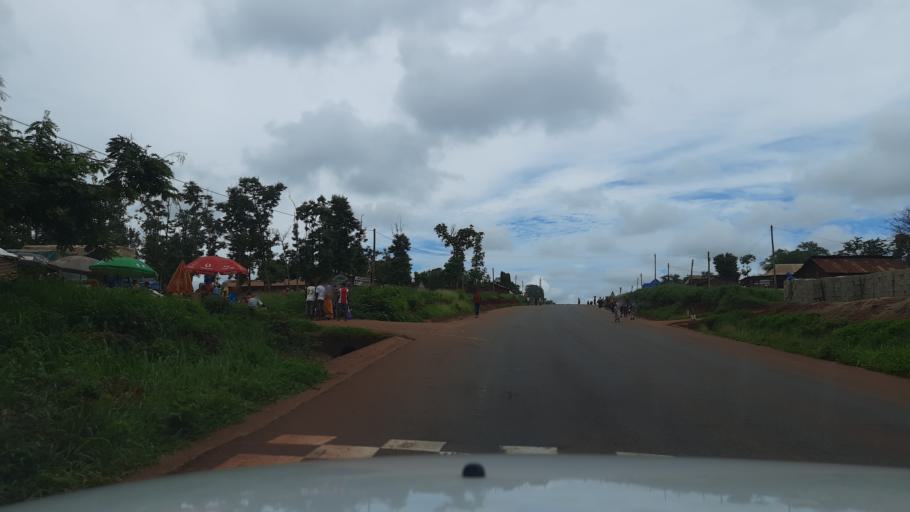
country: TZ
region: Pwani
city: Lugoba
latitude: -6.0835
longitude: 38.2437
